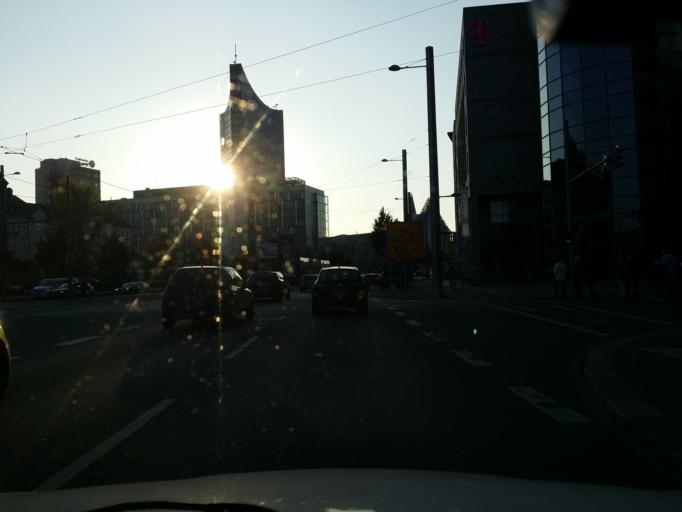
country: DE
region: Saxony
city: Leipzig
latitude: 51.3383
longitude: 12.3853
